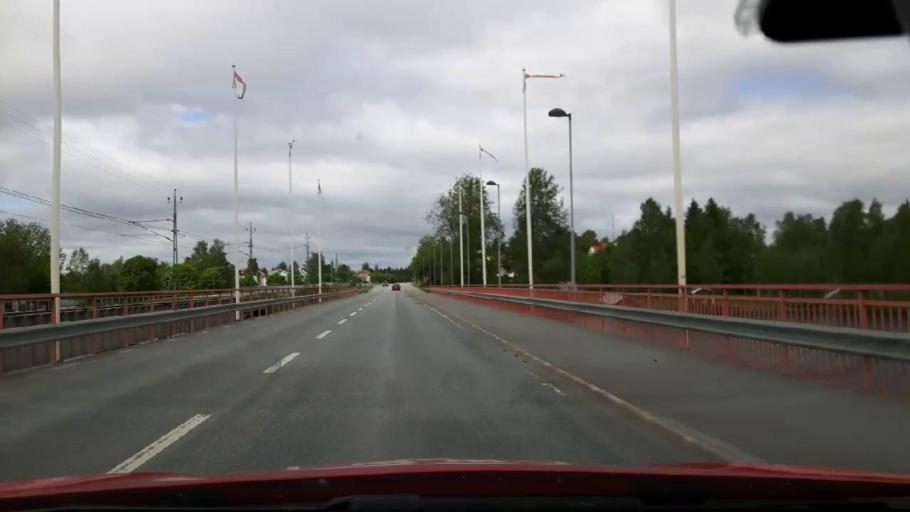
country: SE
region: Jaemtland
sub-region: Krokoms Kommun
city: Krokom
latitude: 63.3229
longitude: 14.4532
